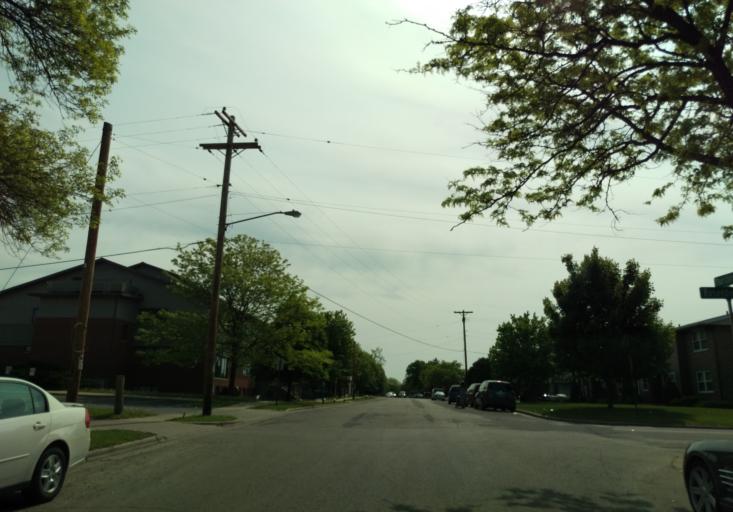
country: US
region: Wisconsin
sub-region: Dane County
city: Shorewood Hills
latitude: 43.0313
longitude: -89.4583
